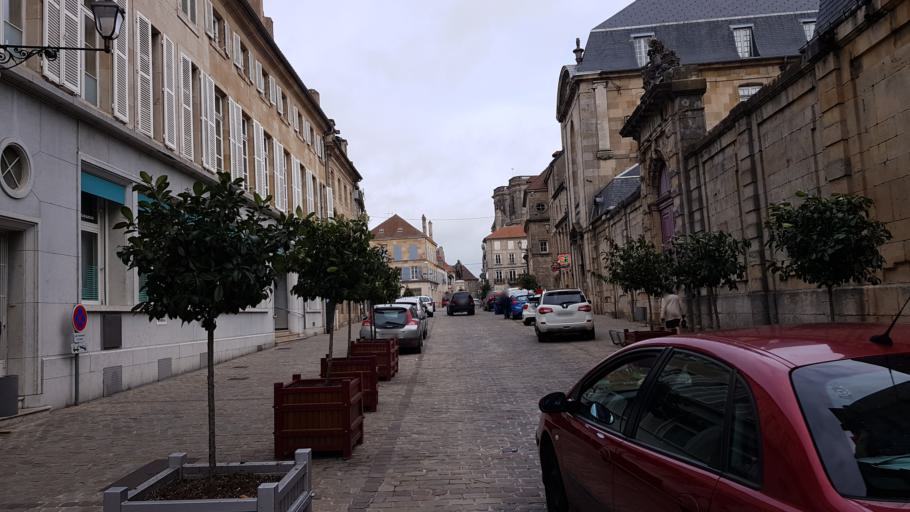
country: FR
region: Champagne-Ardenne
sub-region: Departement de la Haute-Marne
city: Langres
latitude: 47.8619
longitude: 5.3339
